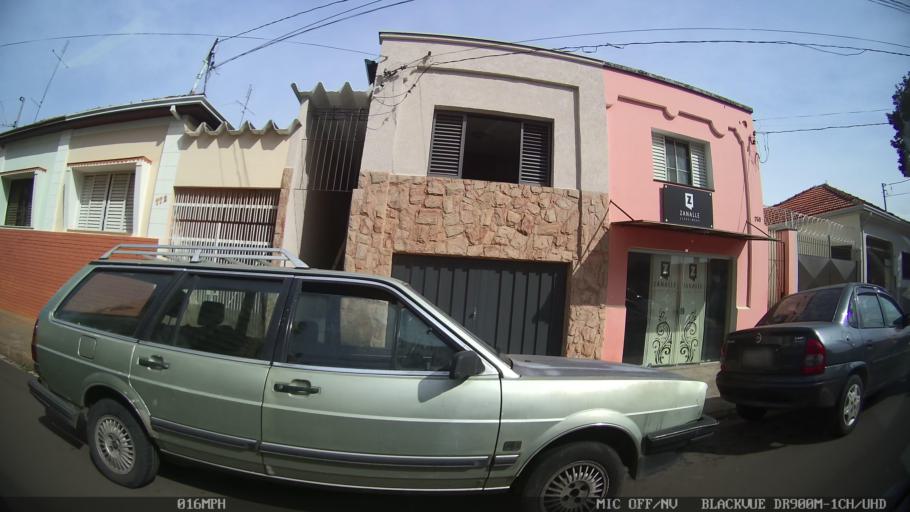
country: BR
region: Sao Paulo
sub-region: Piracicaba
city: Piracicaba
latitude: -22.7373
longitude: -47.6553
